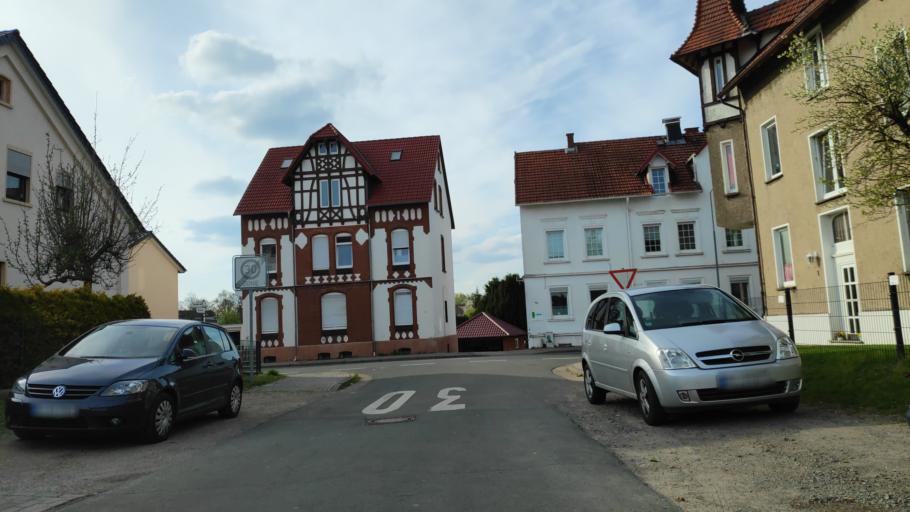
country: DE
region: North Rhine-Westphalia
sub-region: Regierungsbezirk Detmold
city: Minden
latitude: 52.2919
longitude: 8.9459
